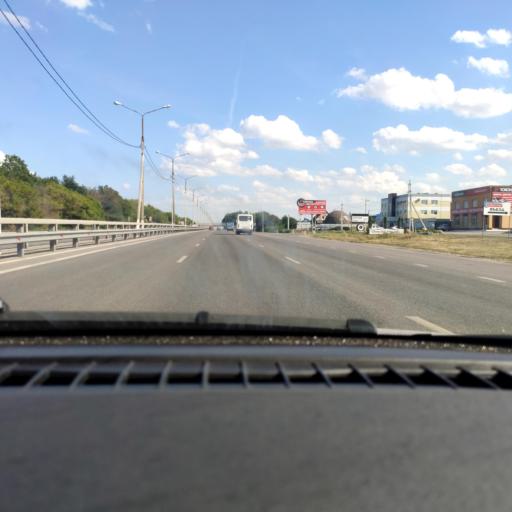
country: RU
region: Voronezj
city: Novaya Usman'
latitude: 51.6340
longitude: 39.3371
